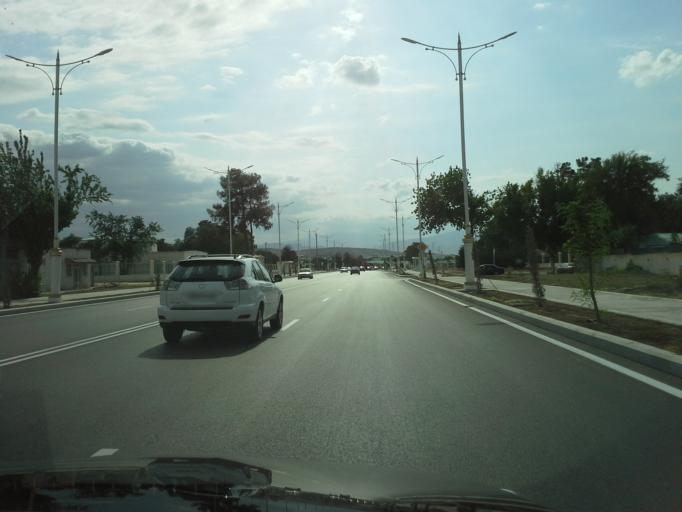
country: TM
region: Ahal
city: Ashgabat
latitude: 37.9583
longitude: 58.3435
